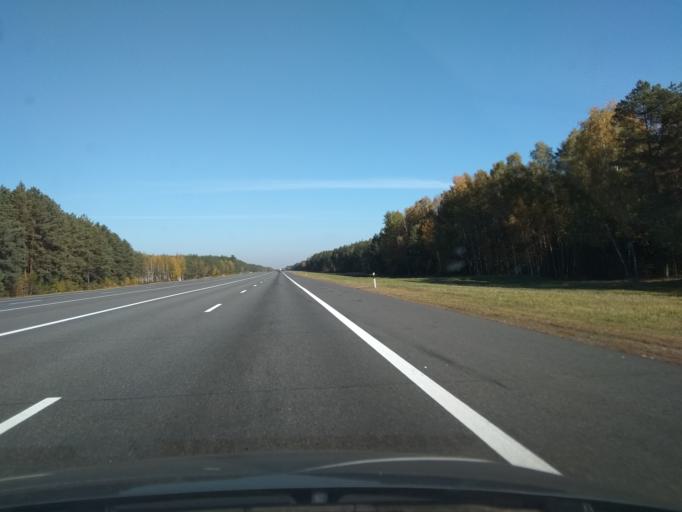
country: BY
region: Brest
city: Ivatsevichy
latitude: 52.7517
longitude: 25.5020
